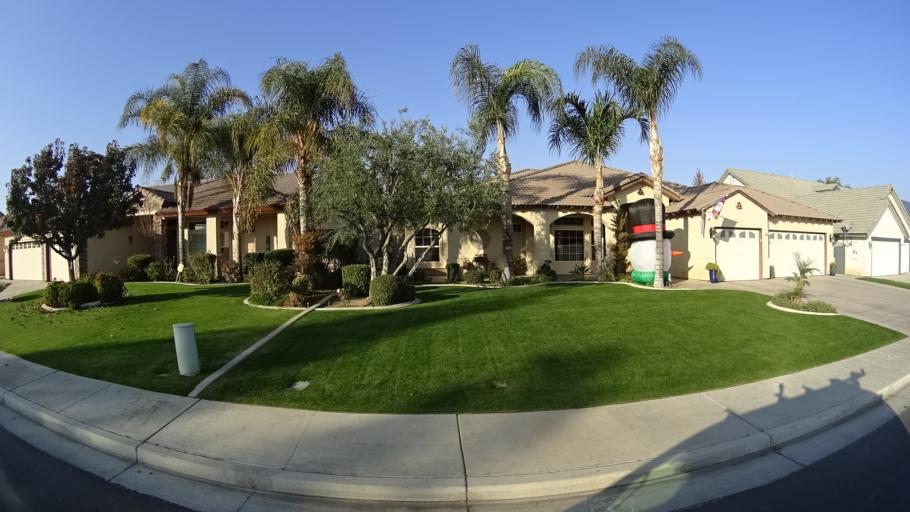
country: US
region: California
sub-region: Kern County
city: Rosedale
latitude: 35.3818
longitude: -119.1506
